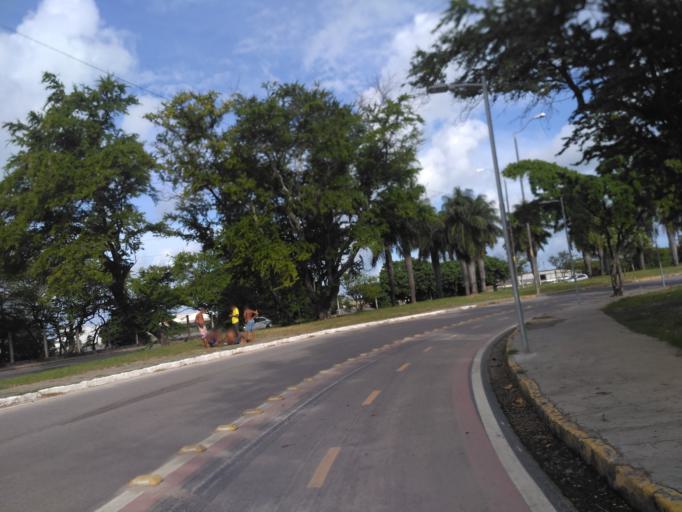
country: BR
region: Pernambuco
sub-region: Recife
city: Recife
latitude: -8.0453
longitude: -34.8741
